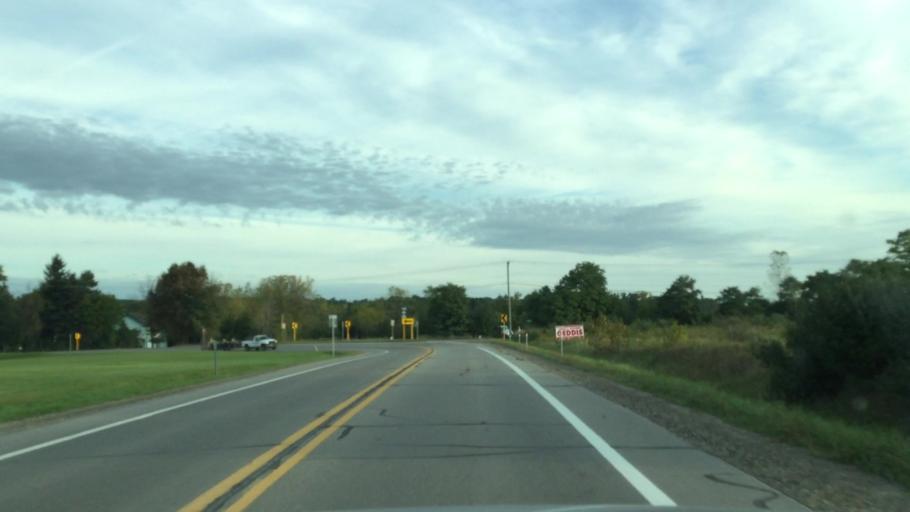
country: US
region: Michigan
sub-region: Livingston County
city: Whitmore Lake
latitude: 42.4512
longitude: -83.7853
